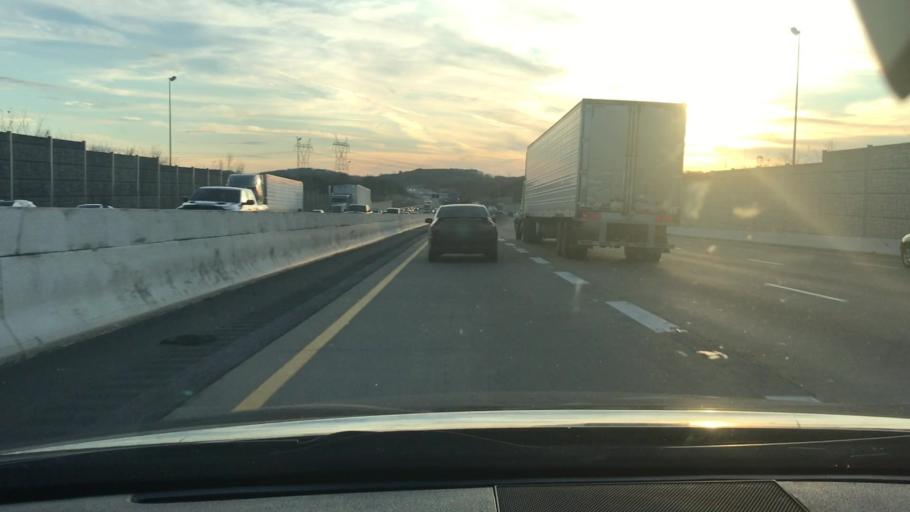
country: US
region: Tennessee
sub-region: Davidson County
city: Goodlettsville
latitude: 36.2953
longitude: -86.7168
